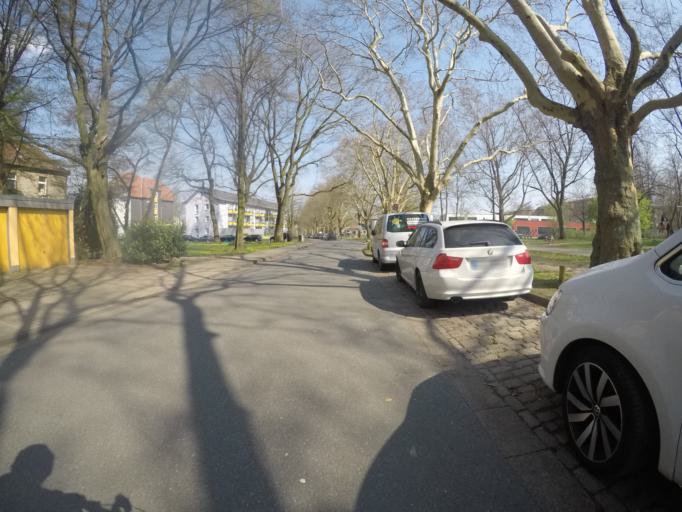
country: DE
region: North Rhine-Westphalia
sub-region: Regierungsbezirk Detmold
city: Bielefeld
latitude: 52.0178
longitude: 8.5484
